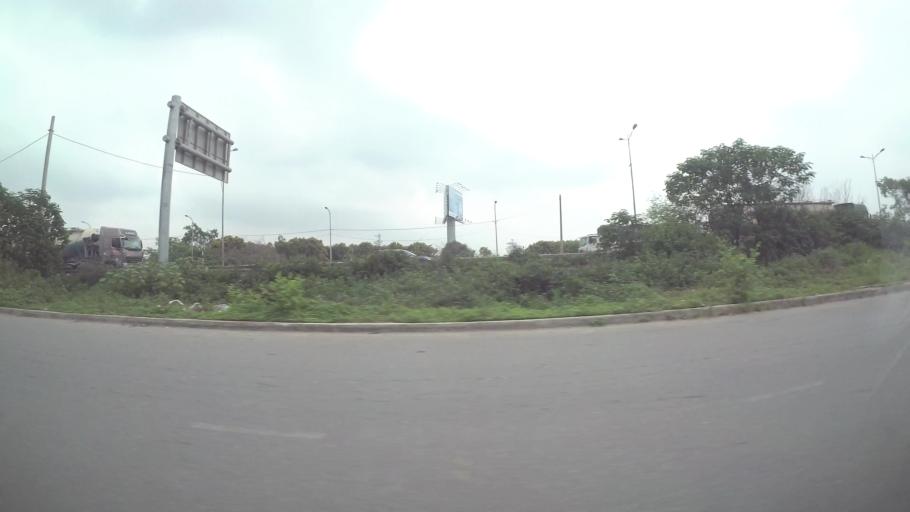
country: VN
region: Ha Noi
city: Trau Quy
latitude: 21.0328
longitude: 105.9325
